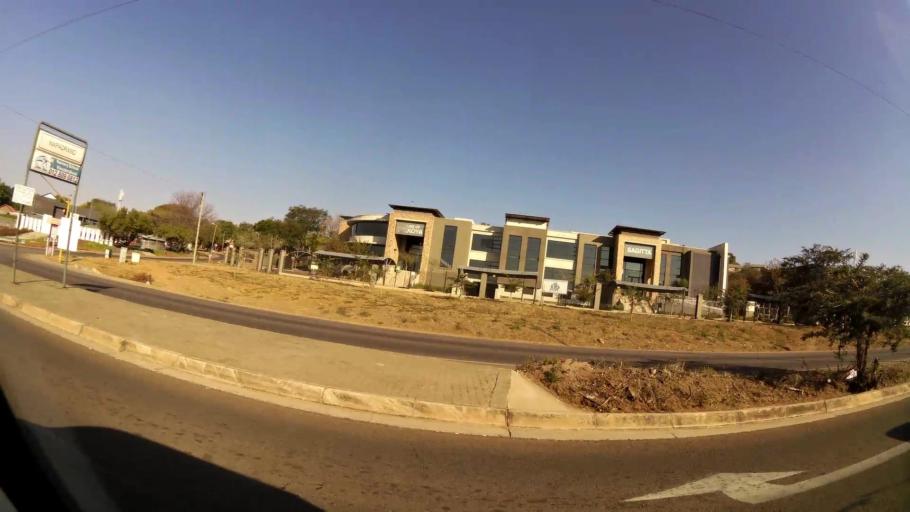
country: ZA
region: Gauteng
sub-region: City of Tshwane Metropolitan Municipality
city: Pretoria
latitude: -25.7810
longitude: 28.3381
